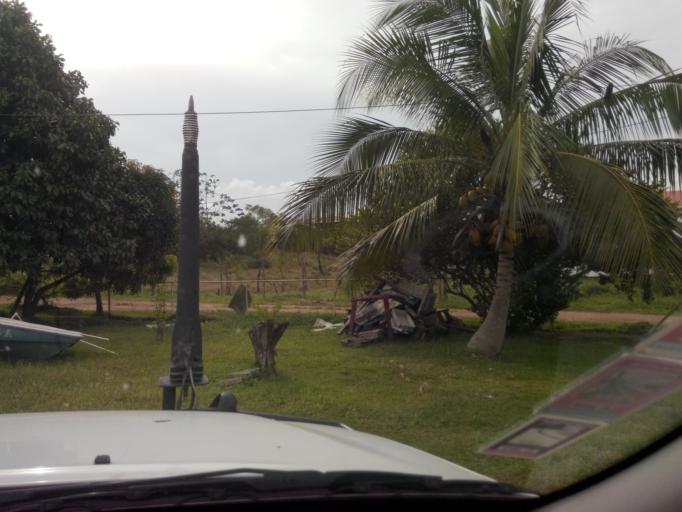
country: NI
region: Atlantico Sur
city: Bluefields
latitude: 12.0316
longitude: -83.7625
